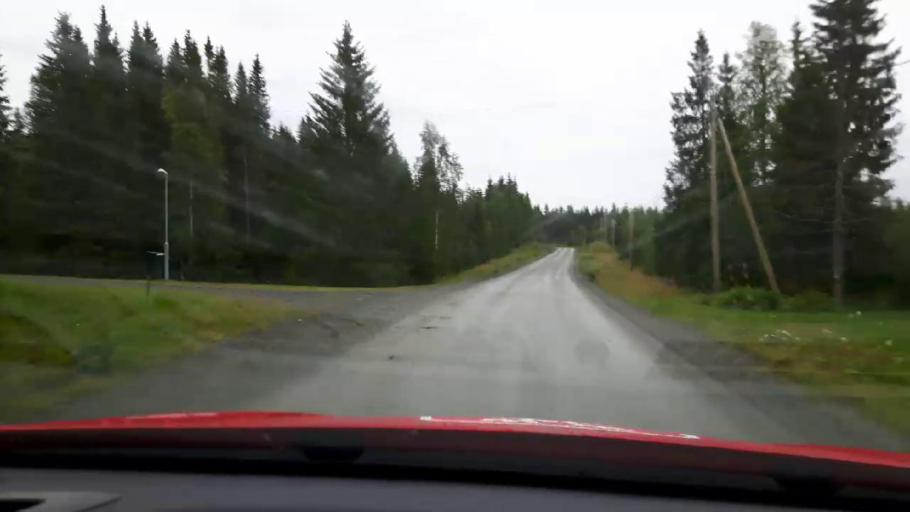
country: SE
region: Jaemtland
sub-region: Are Kommun
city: Are
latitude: 63.4821
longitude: 12.7949
